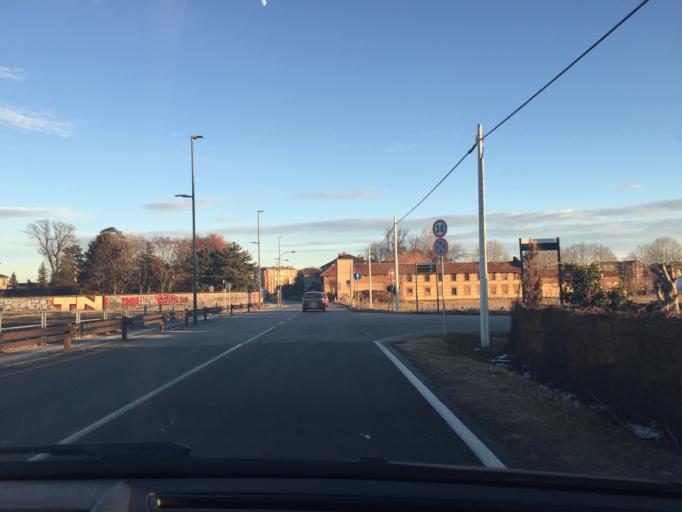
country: IT
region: Piedmont
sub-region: Provincia di Torino
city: Gerbido
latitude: 45.0462
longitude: 7.6101
